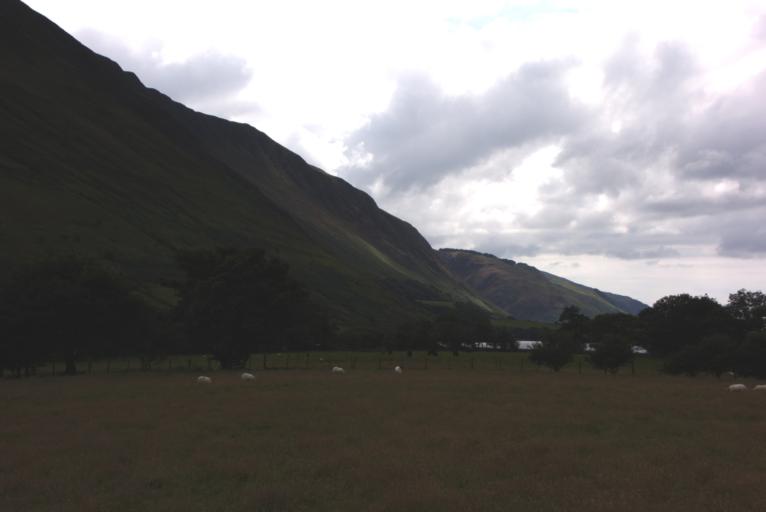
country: GB
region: Wales
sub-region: Gwynedd
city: Corris
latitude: 52.6809
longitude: -3.8823
